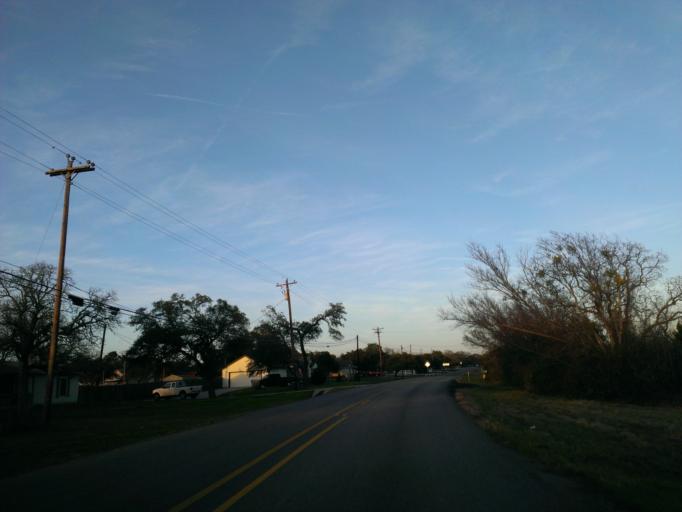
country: US
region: Texas
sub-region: Burnet County
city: Bertram
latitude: 30.7406
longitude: -98.0636
